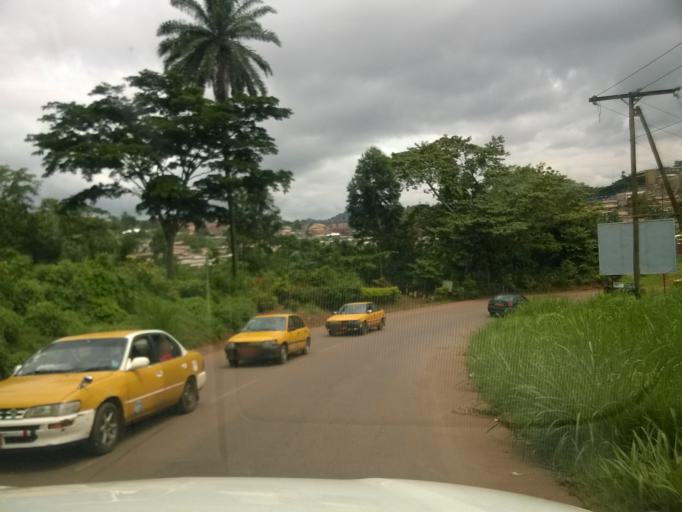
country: CM
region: Centre
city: Yaounde
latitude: 3.8472
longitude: 11.5023
